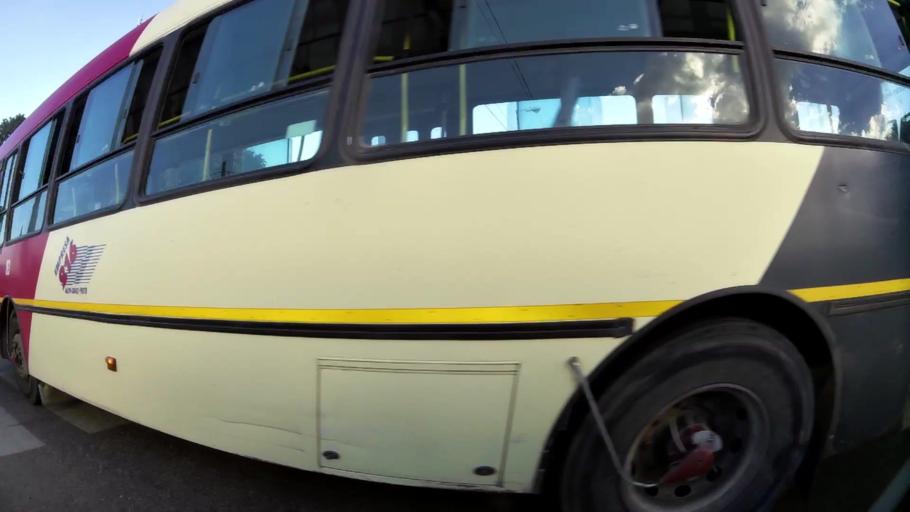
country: AR
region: Buenos Aires
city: Ituzaingo
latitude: -34.6978
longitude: -58.6386
